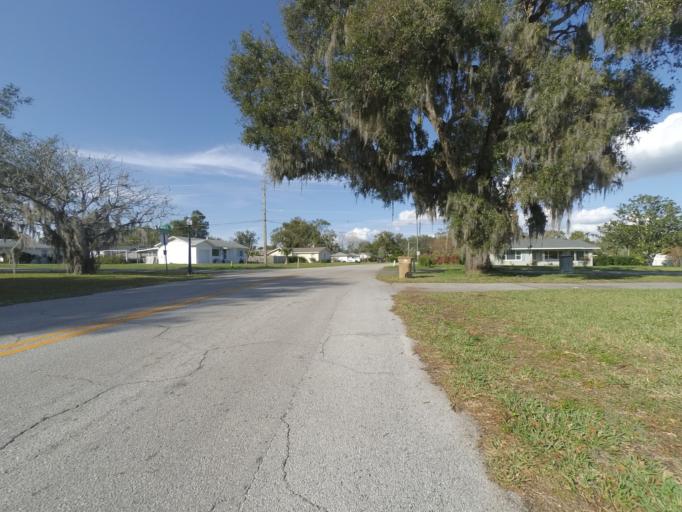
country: US
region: Florida
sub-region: Lake County
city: Mount Dora
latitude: 28.8126
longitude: -81.6647
